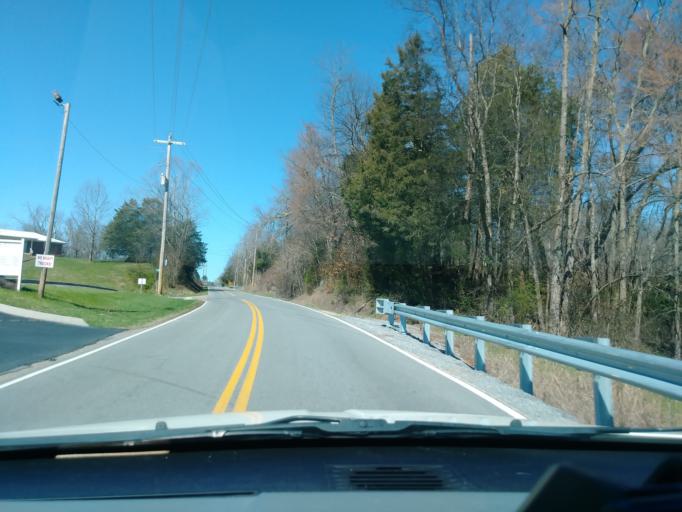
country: US
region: Tennessee
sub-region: Cocke County
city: Newport
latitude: 35.9852
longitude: -83.0604
